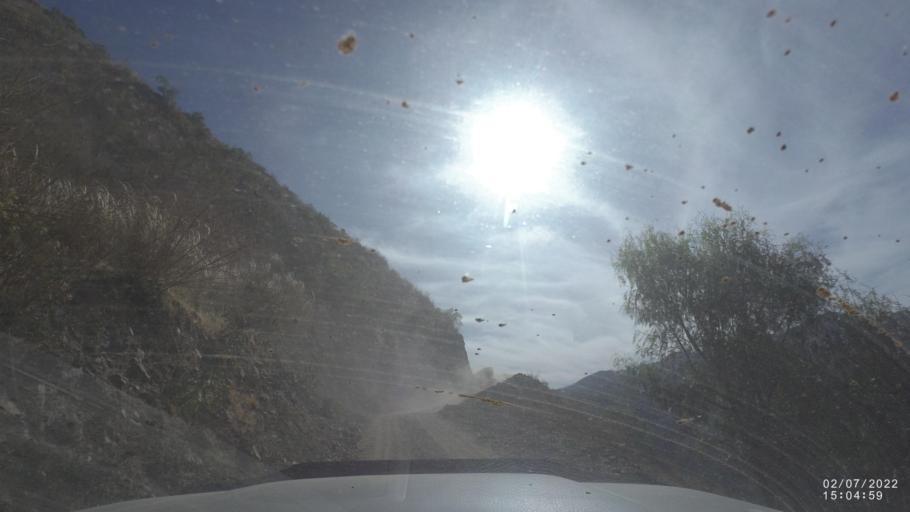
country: BO
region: Cochabamba
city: Irpa Irpa
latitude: -17.8613
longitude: -66.4353
